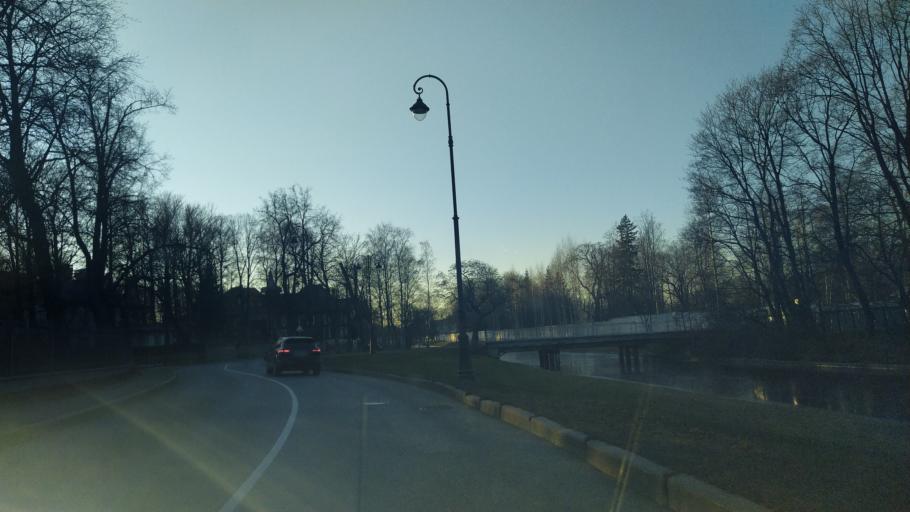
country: RU
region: St.-Petersburg
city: Novaya Derevnya
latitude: 59.9787
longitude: 30.2845
